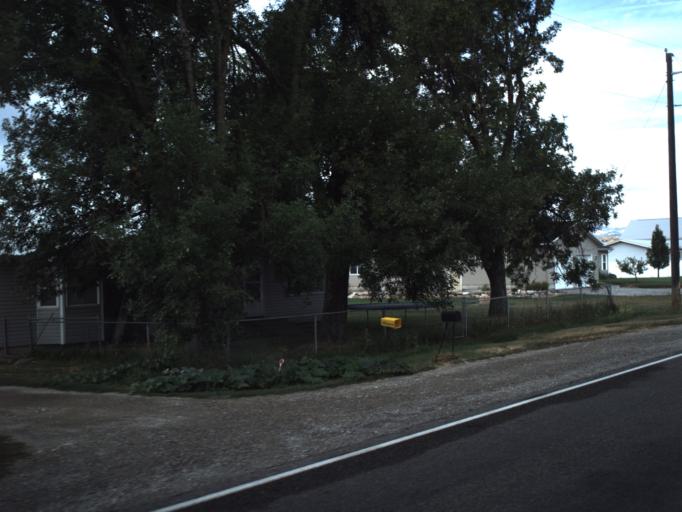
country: US
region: Utah
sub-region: Cache County
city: Lewiston
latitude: 41.9605
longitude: -111.9540
